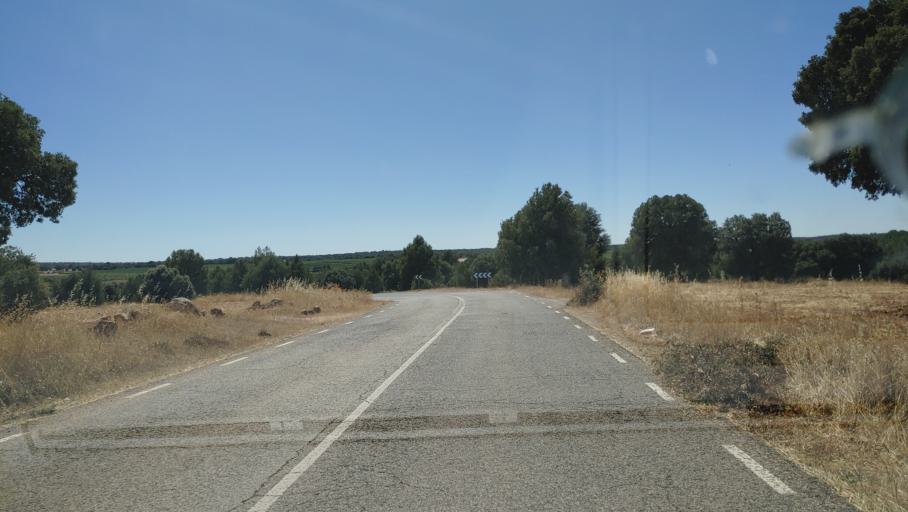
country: ES
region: Castille-La Mancha
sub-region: Provincia de Albacete
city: Ossa de Montiel
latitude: 38.9035
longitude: -2.7616
